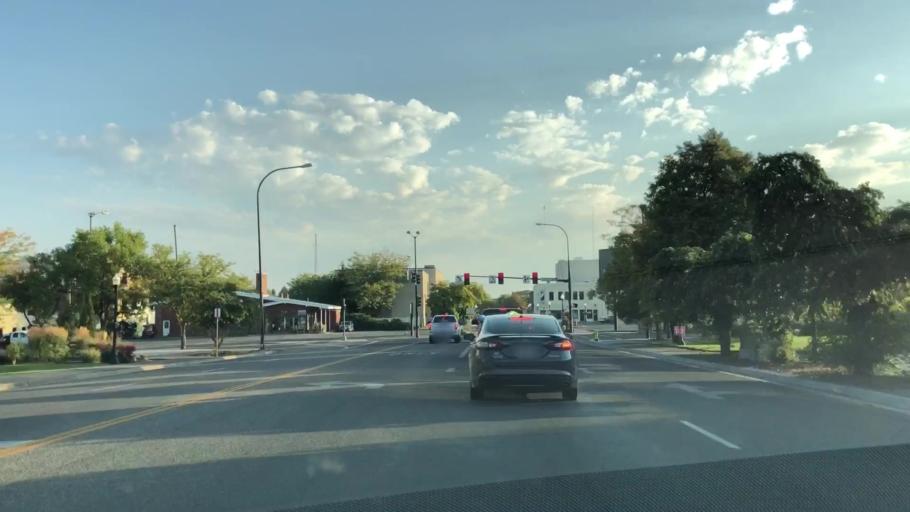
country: US
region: Idaho
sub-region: Bonneville County
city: Idaho Falls
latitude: 43.4916
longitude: -112.0431
